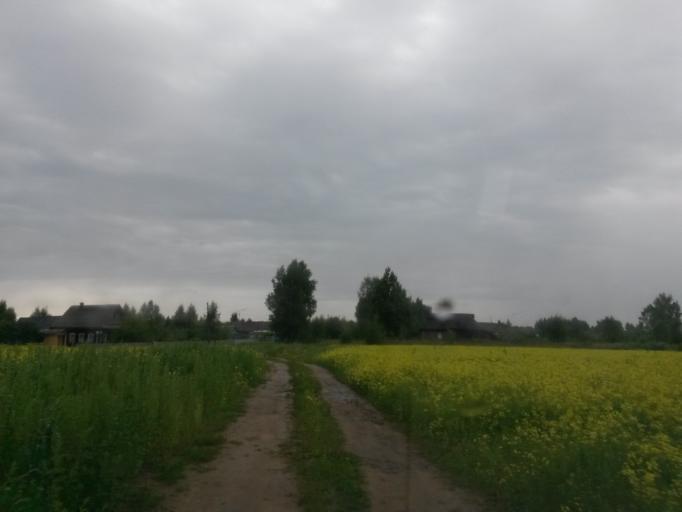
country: RU
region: Jaroslavl
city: Tutayev
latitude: 57.9438
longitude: 39.4410
